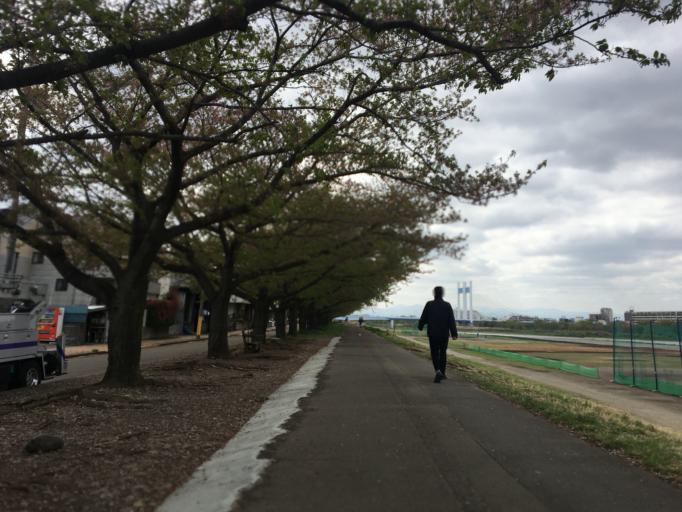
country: JP
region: Tokyo
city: Chofugaoka
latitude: 35.6510
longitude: 139.4967
